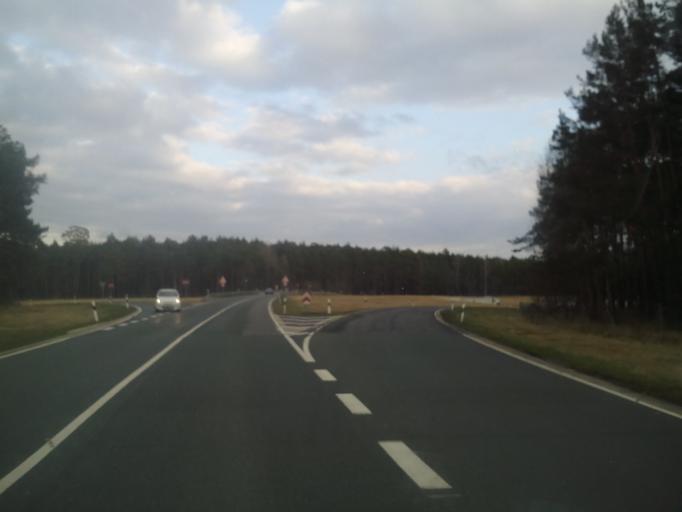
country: DE
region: Bavaria
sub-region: Upper Franconia
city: Pommersfelden
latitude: 49.7441
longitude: 10.8257
